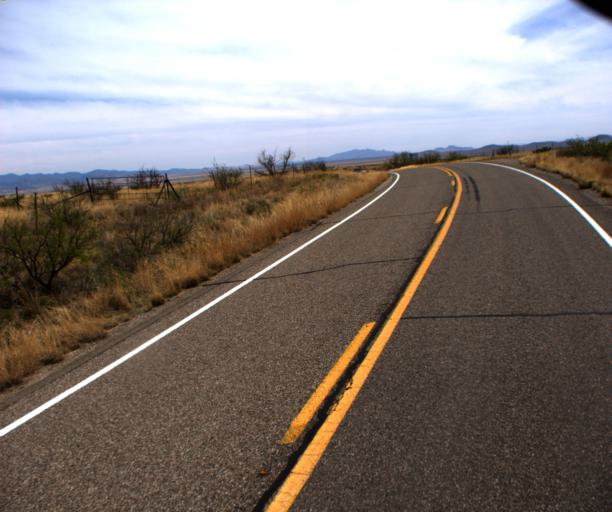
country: US
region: Arizona
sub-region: Cochise County
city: Willcox
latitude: 32.1435
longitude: -109.5654
